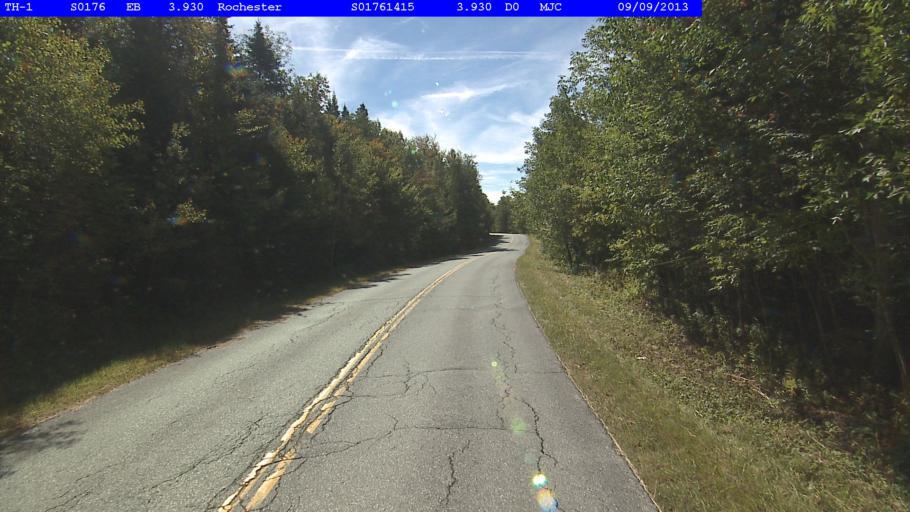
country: US
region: Vermont
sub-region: Orange County
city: Randolph
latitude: 43.8515
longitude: -72.7514
